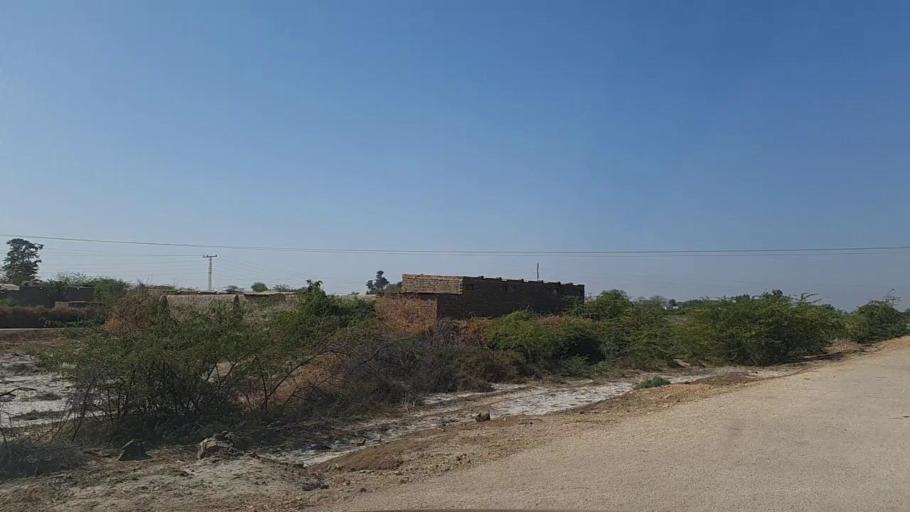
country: PK
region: Sindh
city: Pithoro
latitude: 25.4372
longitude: 69.3734
